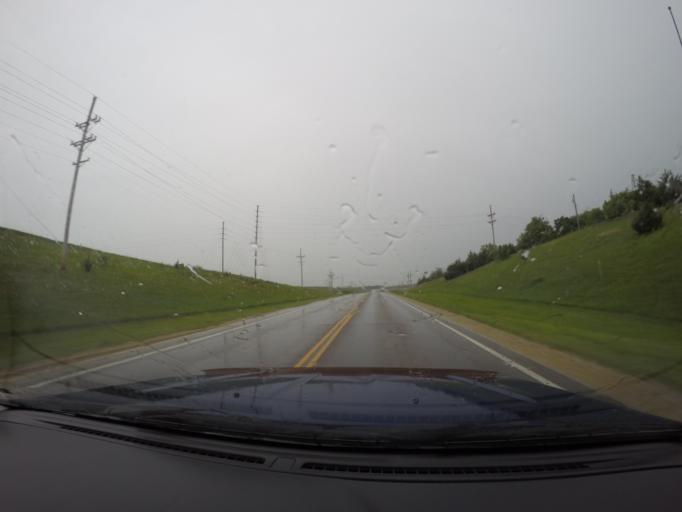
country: US
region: Kansas
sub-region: Cloud County
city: Concordia
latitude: 39.5738
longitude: -97.6915
